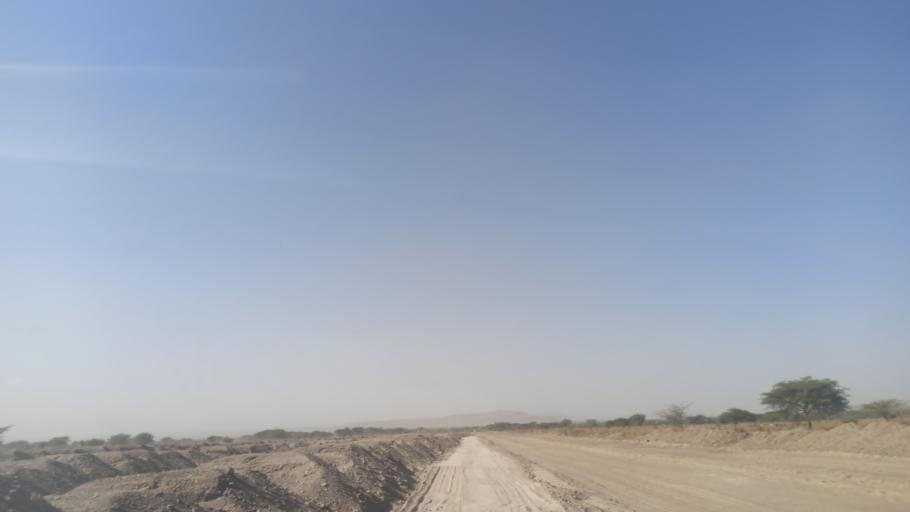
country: ET
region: Oromiya
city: Ziway
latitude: 7.7427
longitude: 38.6190
